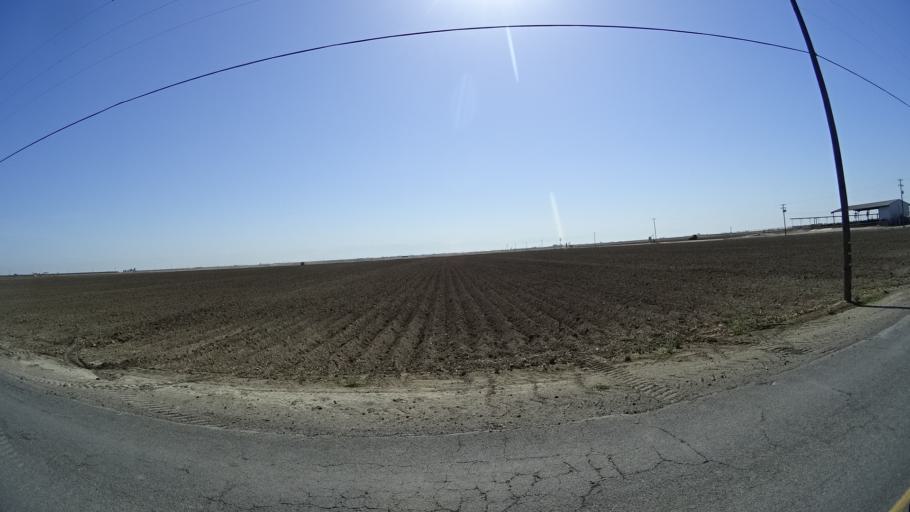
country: US
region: California
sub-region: Kings County
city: Home Garden
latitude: 36.2489
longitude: -119.5473
